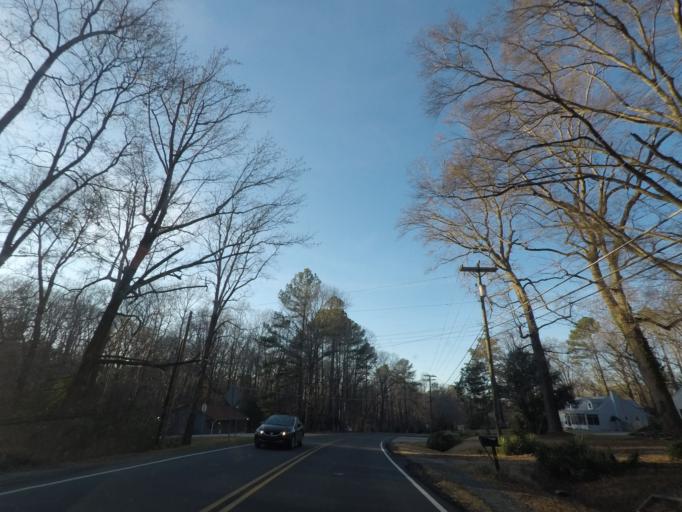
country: US
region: North Carolina
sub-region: Durham County
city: Durham
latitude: 36.0455
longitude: -78.9672
